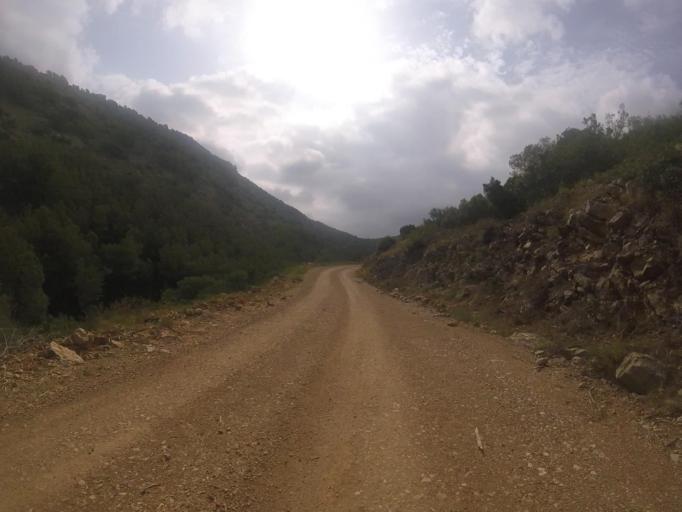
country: ES
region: Valencia
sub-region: Provincia de Castello
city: Santa Magdalena de Pulpis
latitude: 40.3481
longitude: 0.3125
